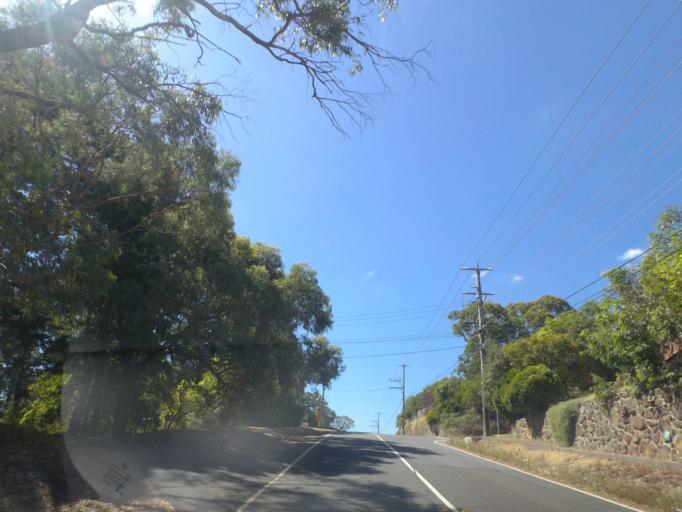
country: AU
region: Victoria
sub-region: Manningham
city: Park Orchards
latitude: -37.7996
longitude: 145.2157
